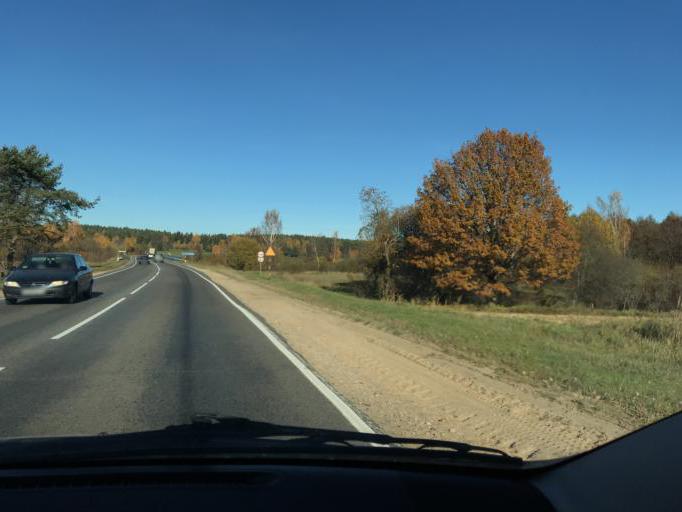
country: BY
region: Vitebsk
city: Polatsk
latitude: 55.3104
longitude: 28.7780
